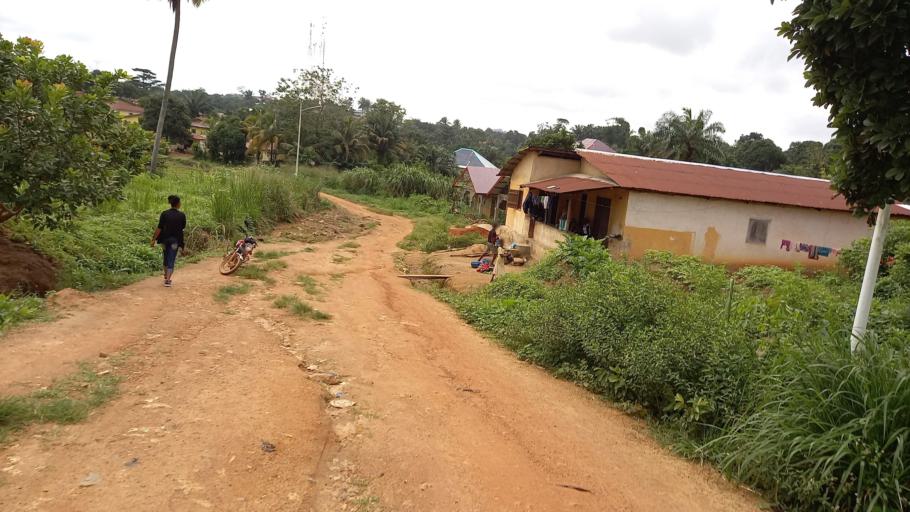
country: SL
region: Eastern Province
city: Kailahun
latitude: 8.2843
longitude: -10.5731
